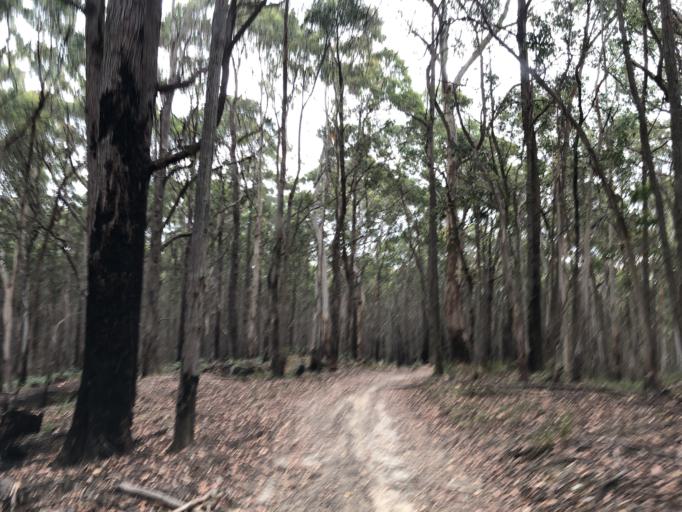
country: AU
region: Victoria
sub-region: Moorabool
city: Bacchus Marsh
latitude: -37.4428
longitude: 144.3353
